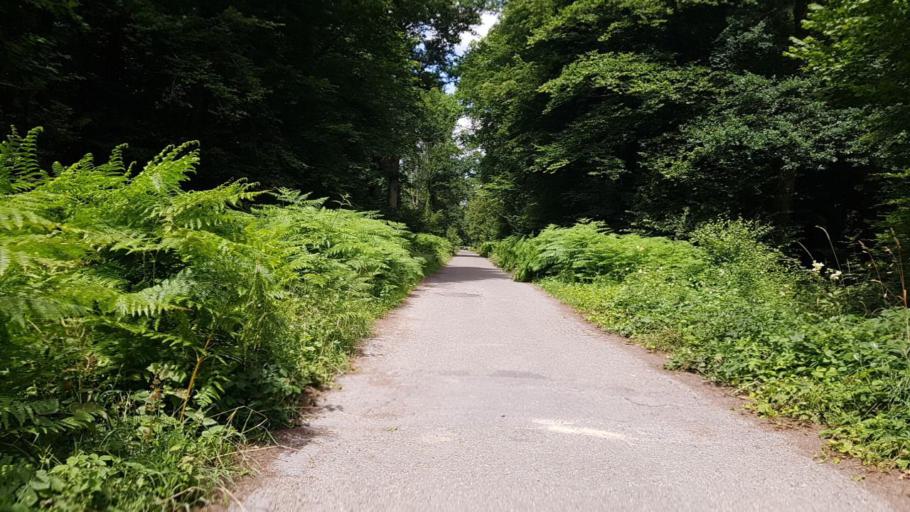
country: FR
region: Picardie
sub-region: Departement de l'Oise
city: Montmacq
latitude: 49.4733
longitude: 2.9185
